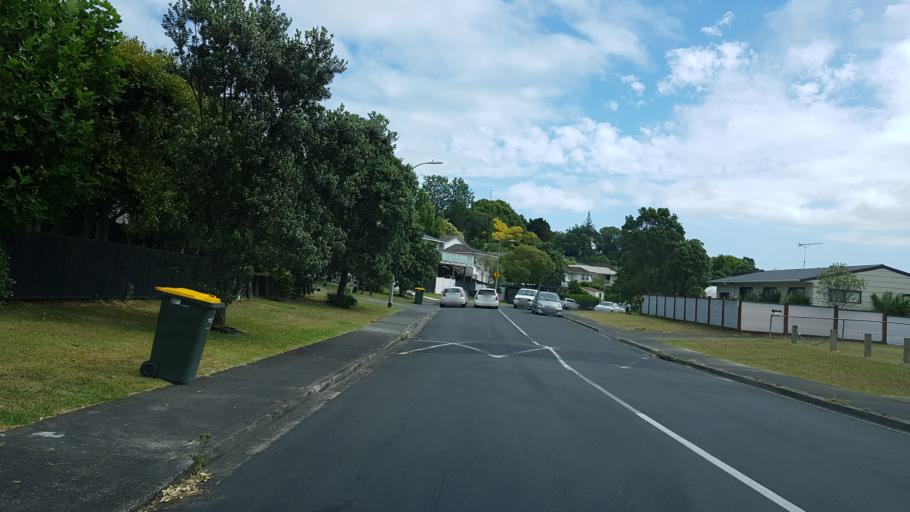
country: NZ
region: Auckland
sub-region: Auckland
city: North Shore
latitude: -36.7704
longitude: 174.7178
